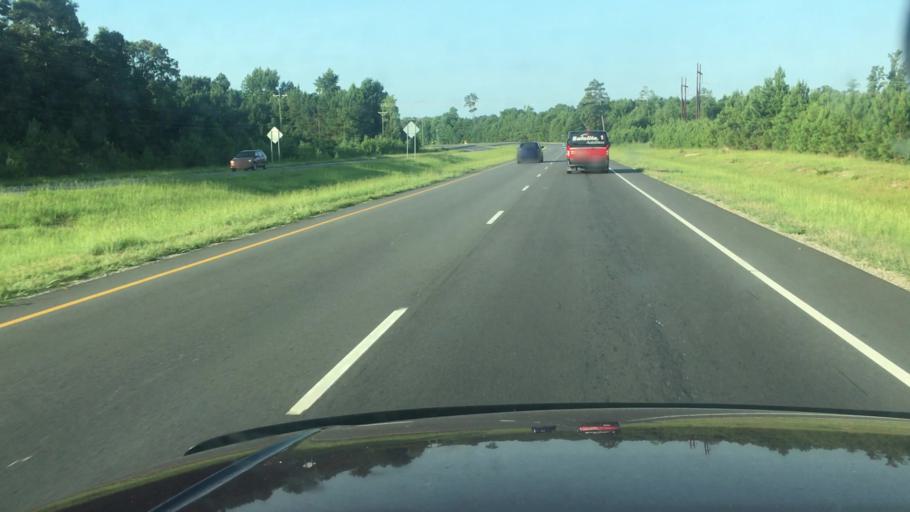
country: US
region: North Carolina
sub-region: Cumberland County
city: Vander
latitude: 34.9480
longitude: -78.8457
